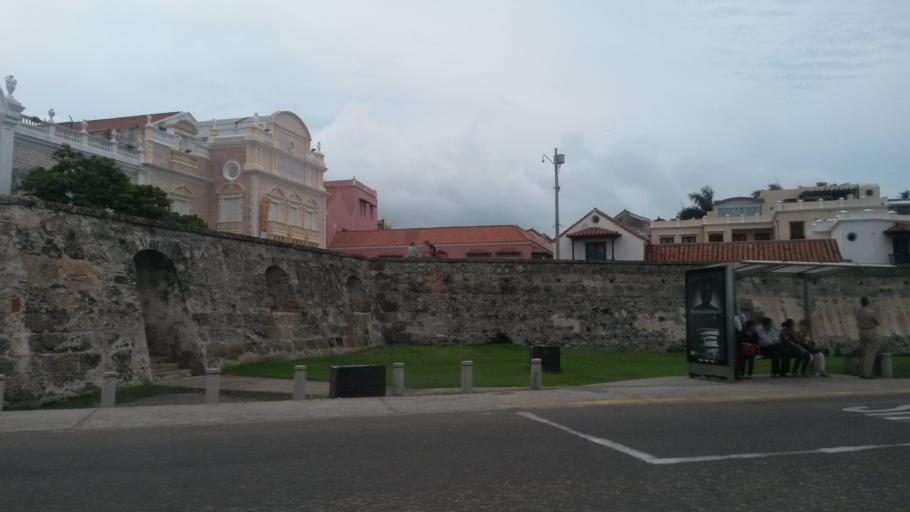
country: CO
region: Bolivar
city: Cartagena
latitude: 10.4272
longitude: -75.5515
